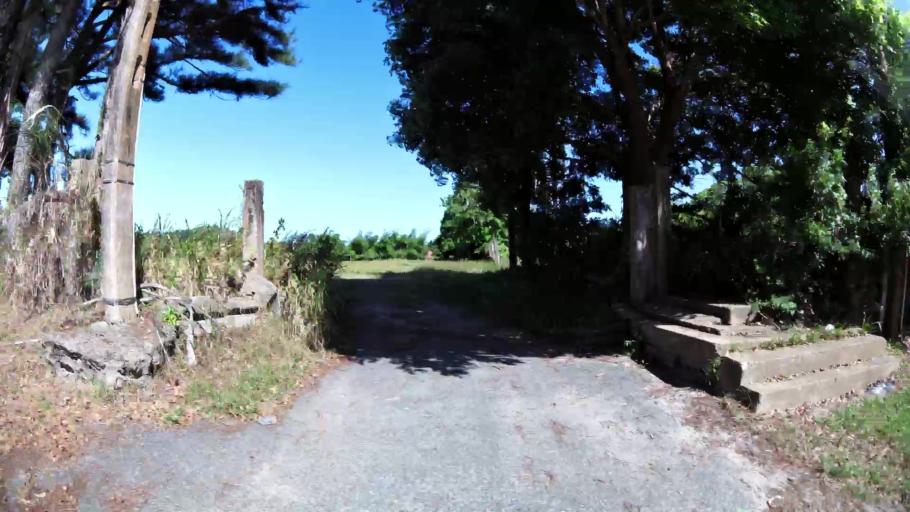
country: GF
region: Guyane
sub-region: Guyane
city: Remire-Montjoly
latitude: 4.9139
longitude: -52.2673
